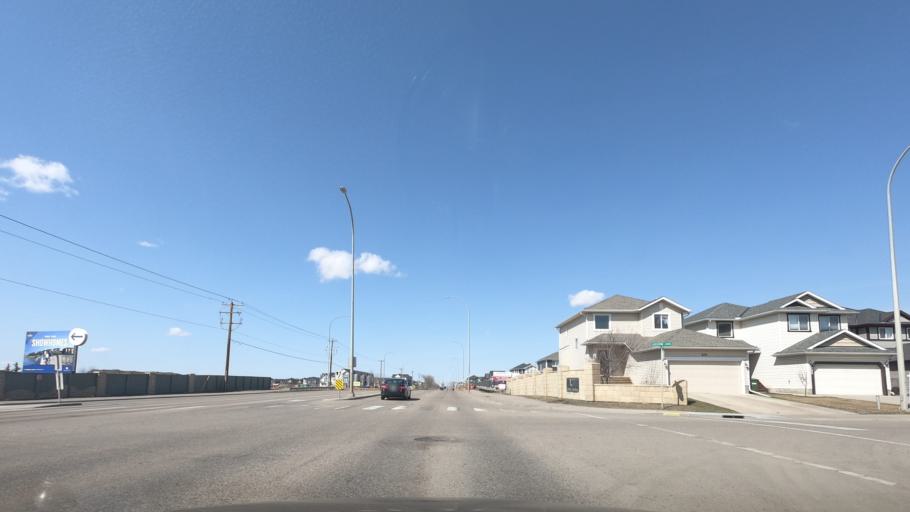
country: CA
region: Alberta
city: Airdrie
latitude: 51.2786
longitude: -114.0251
